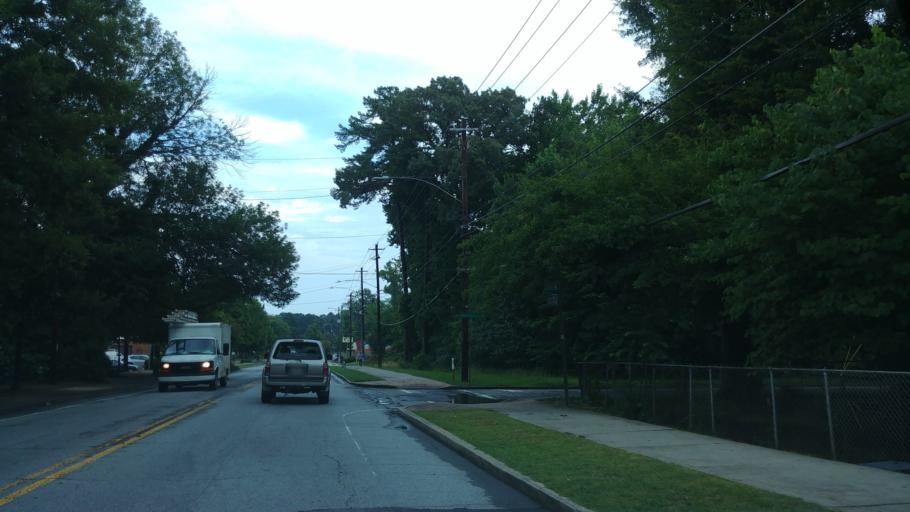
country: US
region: Georgia
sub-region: DeKalb County
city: Chamblee
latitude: 33.8918
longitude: -84.2929
